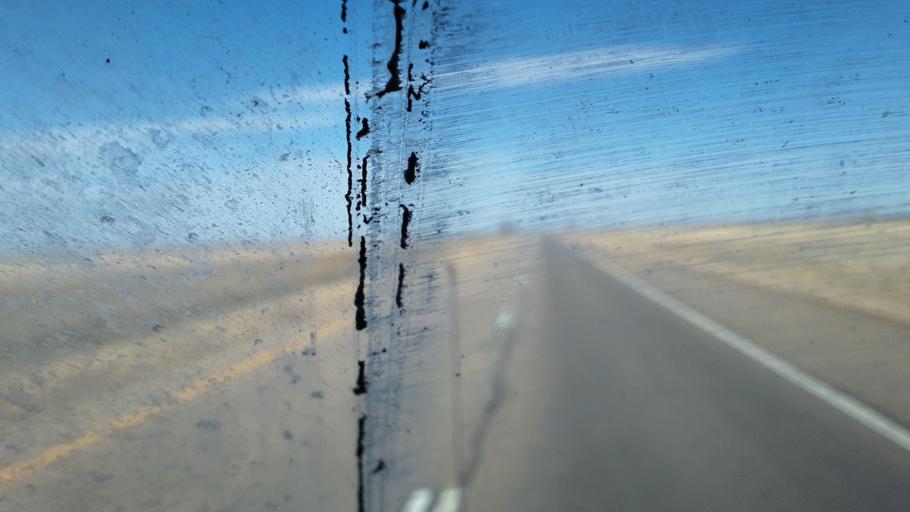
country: US
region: Colorado
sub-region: Weld County
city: Keenesburg
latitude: 40.1388
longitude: -104.4793
